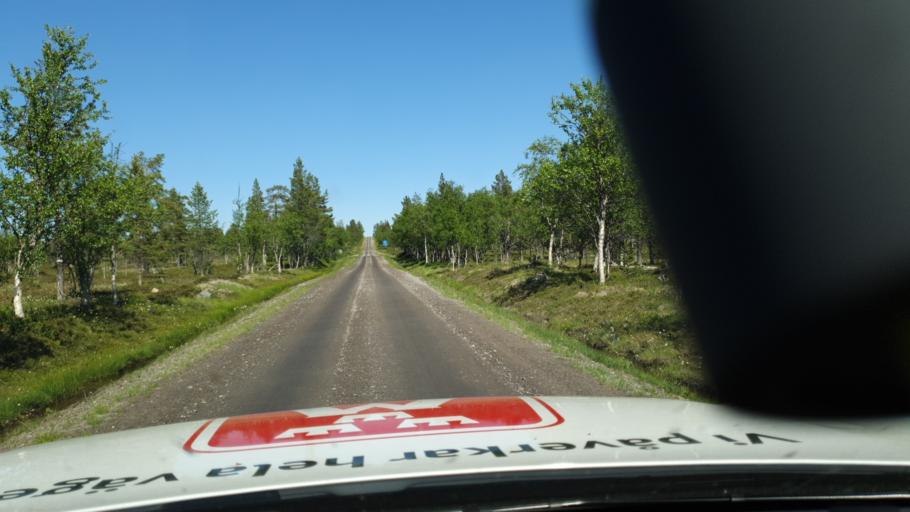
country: NO
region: Hedmark
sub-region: Engerdal
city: Engerdal
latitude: 62.1351
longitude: 12.9263
